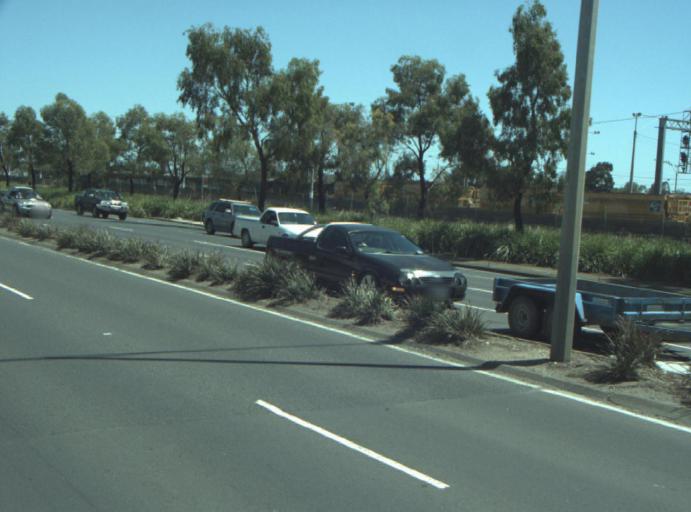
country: AU
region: Victoria
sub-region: Greater Geelong
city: Bell Park
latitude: -38.1151
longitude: 144.3546
